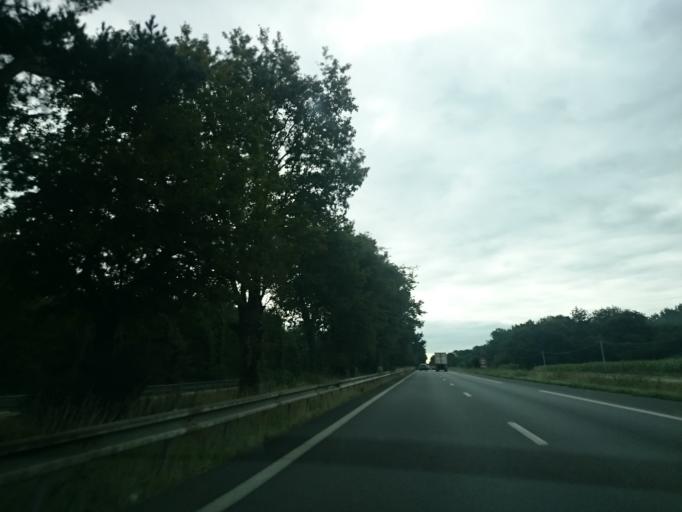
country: FR
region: Brittany
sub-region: Departement du Morbihan
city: Landaul
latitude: 47.7441
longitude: -3.1014
